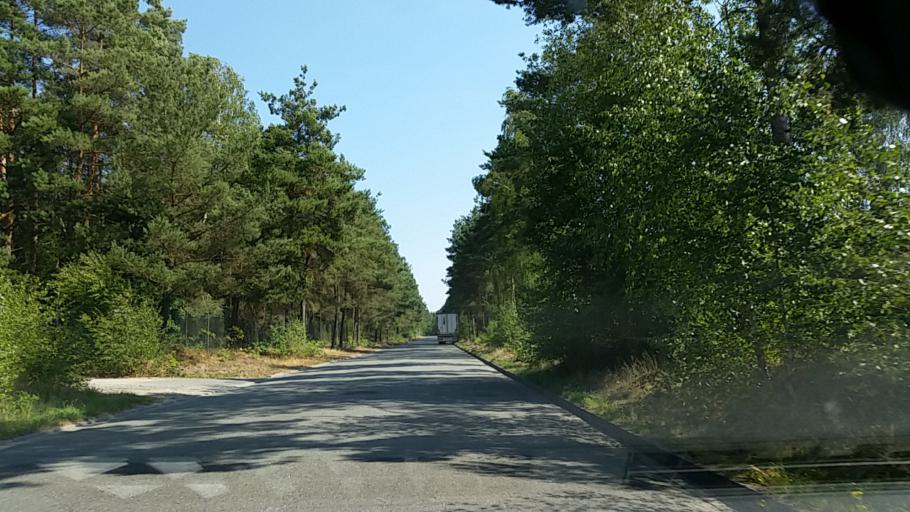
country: DE
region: Lower Saxony
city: Emmendorf
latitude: 53.0041
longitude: 10.5610
